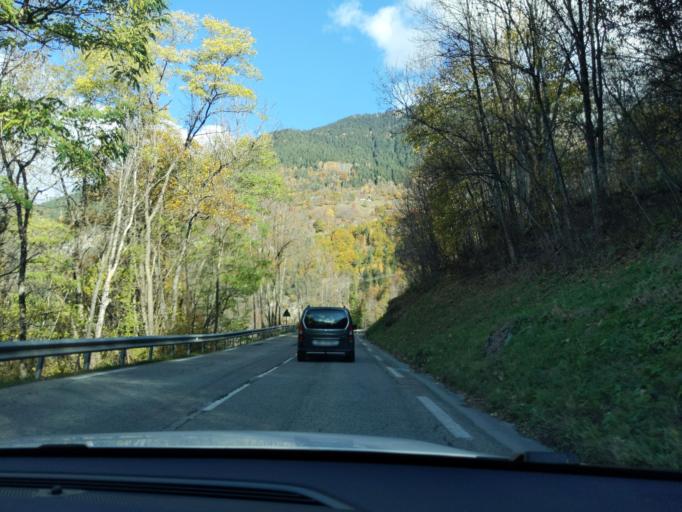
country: FR
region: Rhone-Alpes
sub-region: Departement de la Savoie
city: Seez
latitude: 45.5937
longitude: 6.8815
